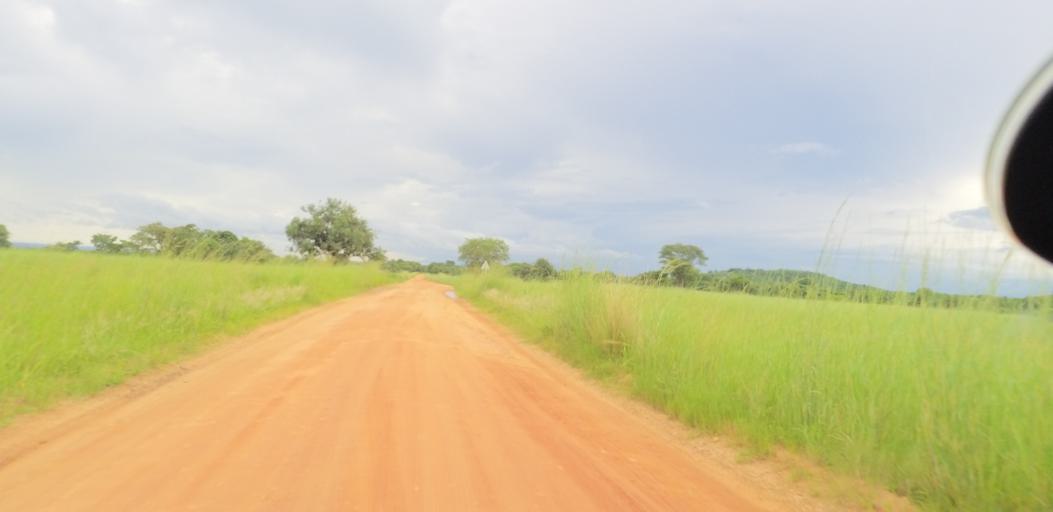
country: ZM
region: Lusaka
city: Chongwe
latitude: -15.1728
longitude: 28.4683
